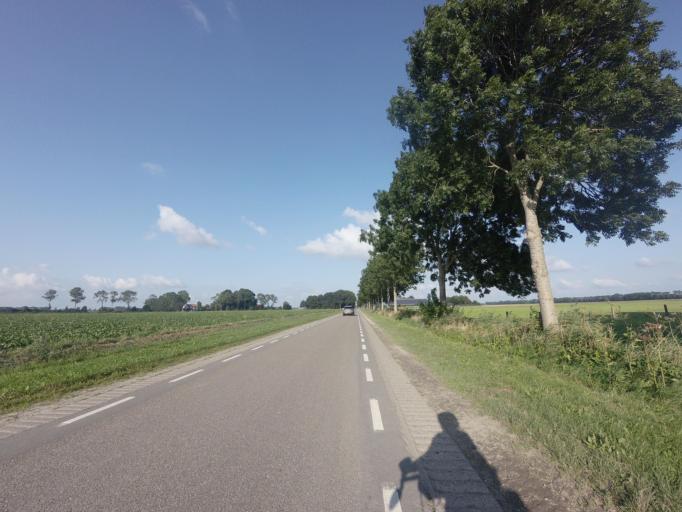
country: NL
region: Flevoland
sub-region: Gemeente Noordoostpolder
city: Ens
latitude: 52.6833
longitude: 5.8325
